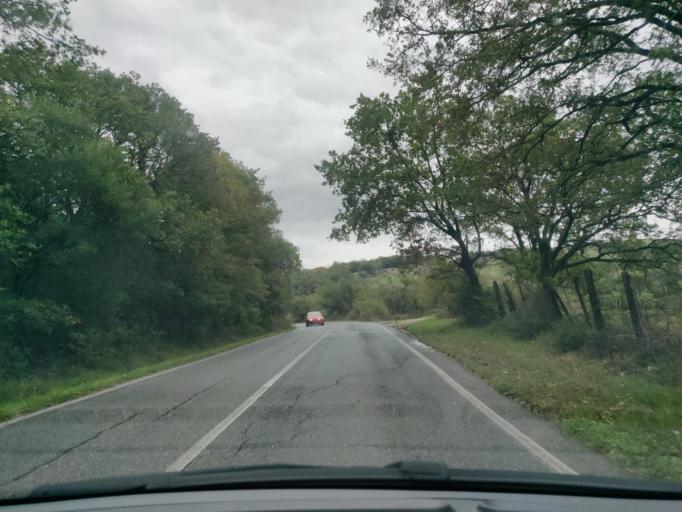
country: IT
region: Latium
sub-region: Citta metropolitana di Roma Capitale
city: Allumiere
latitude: 42.1364
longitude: 11.8711
